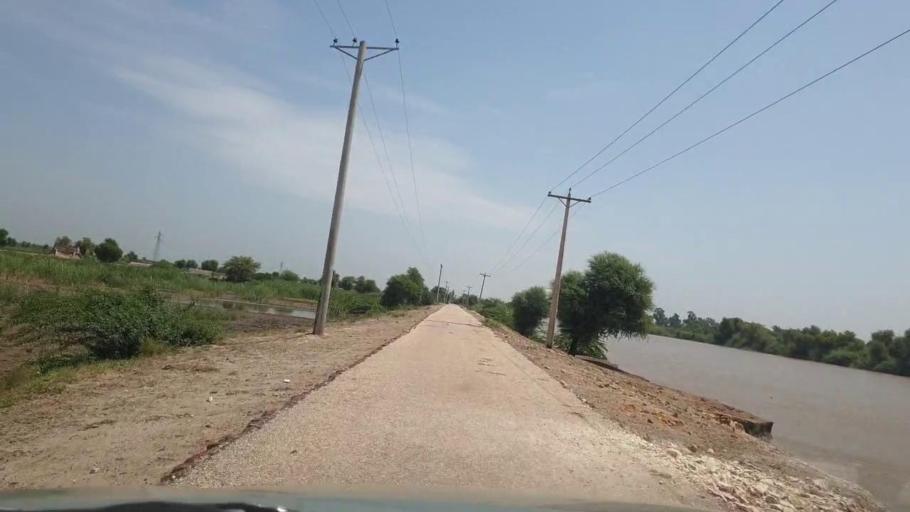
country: PK
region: Sindh
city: Bozdar
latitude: 27.1171
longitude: 68.9906
